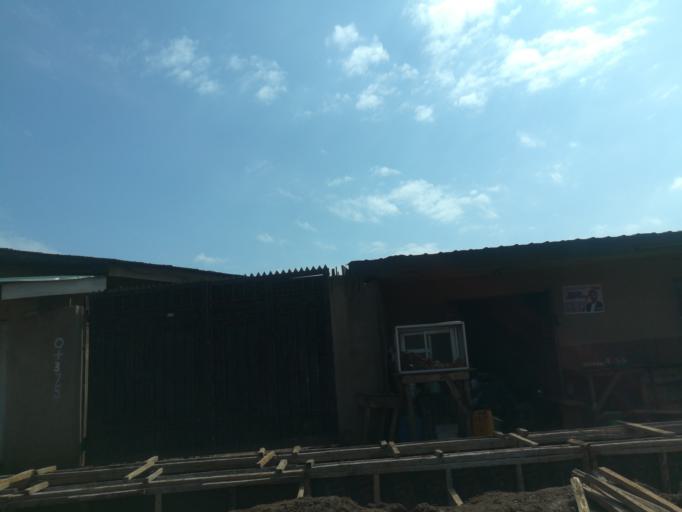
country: NG
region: Oyo
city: Egbeda
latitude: 7.4158
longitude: 3.9786
